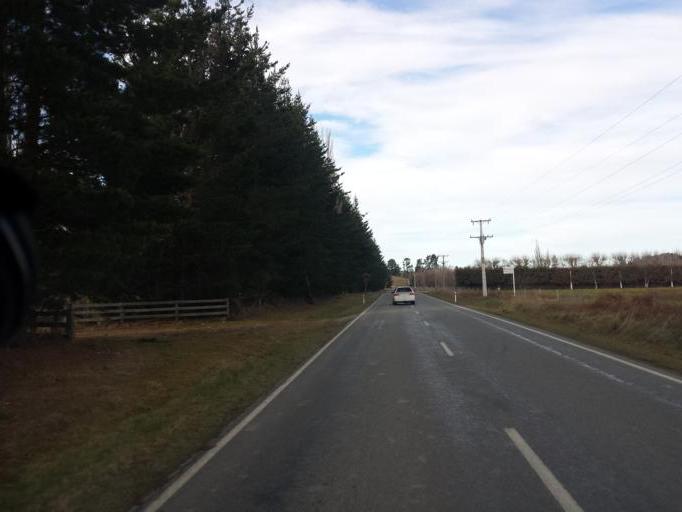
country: NZ
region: Canterbury
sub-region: Timaru District
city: Pleasant Point
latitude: -44.0611
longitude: 170.9375
